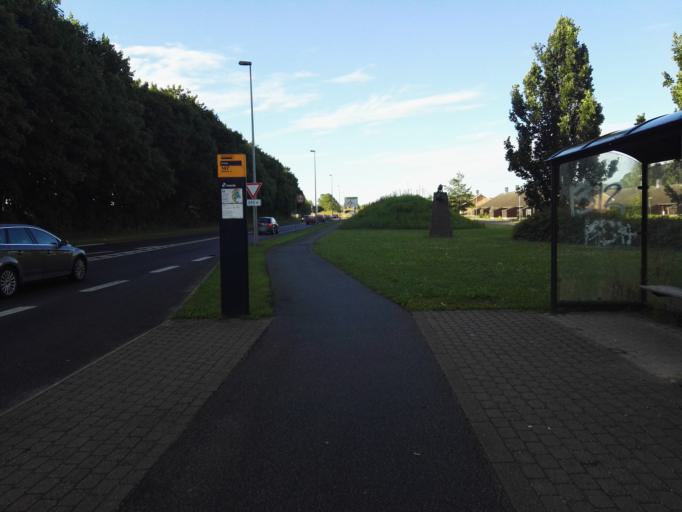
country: DK
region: Capital Region
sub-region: Egedal Kommune
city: Smorumnedre
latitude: 55.7318
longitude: 12.3097
